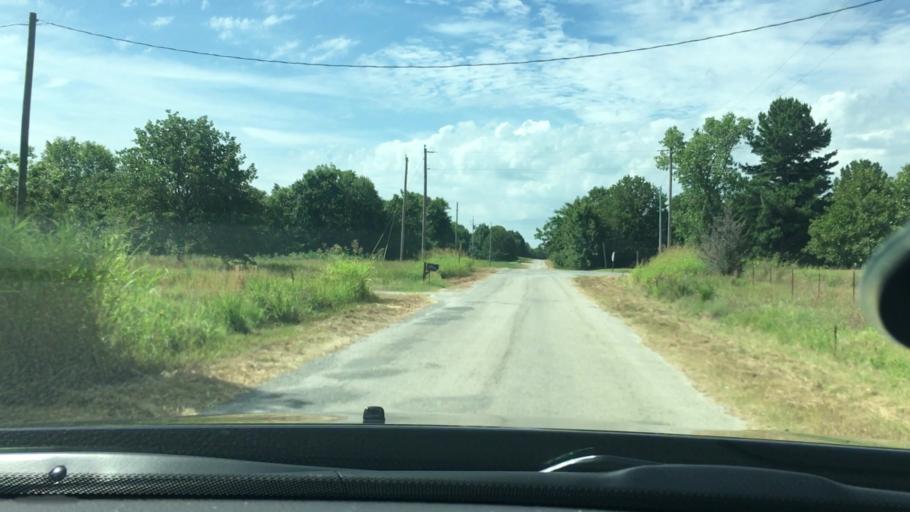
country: US
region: Oklahoma
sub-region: Pontotoc County
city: Ada
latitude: 34.7642
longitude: -96.5650
